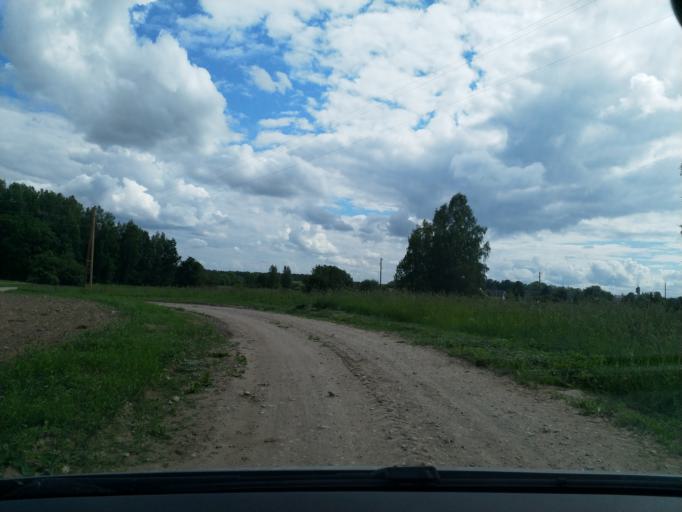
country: LV
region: Kuldigas Rajons
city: Kuldiga
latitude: 56.8477
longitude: 21.9466
